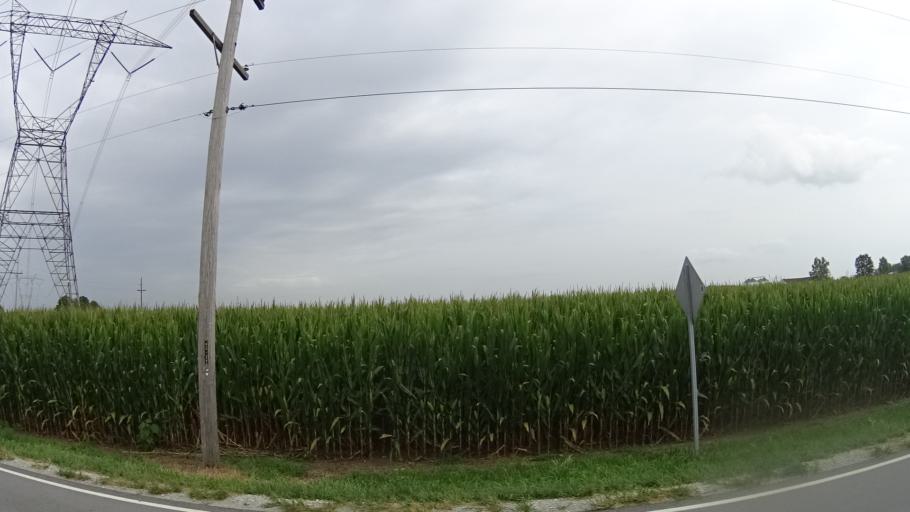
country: US
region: Indiana
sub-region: Madison County
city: Lapel
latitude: 40.0186
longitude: -85.8377
